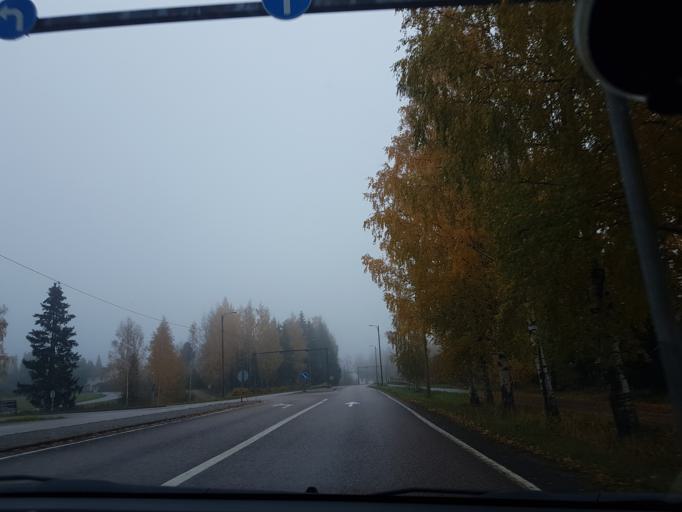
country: FI
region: Uusimaa
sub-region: Helsinki
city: Tuusula
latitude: 60.4101
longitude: 25.0416
